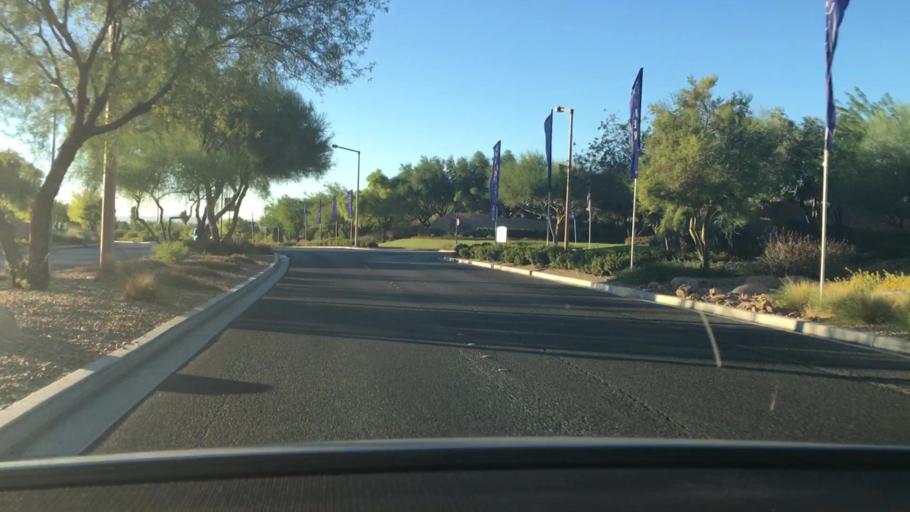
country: US
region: Nevada
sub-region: Clark County
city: Summerlin South
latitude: 36.1269
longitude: -115.3404
